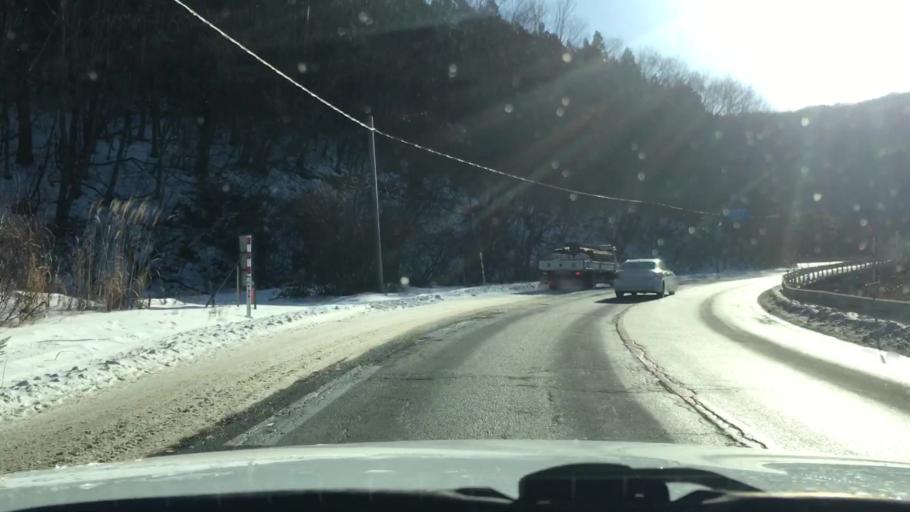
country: JP
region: Iwate
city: Morioka-shi
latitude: 39.6576
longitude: 141.3398
